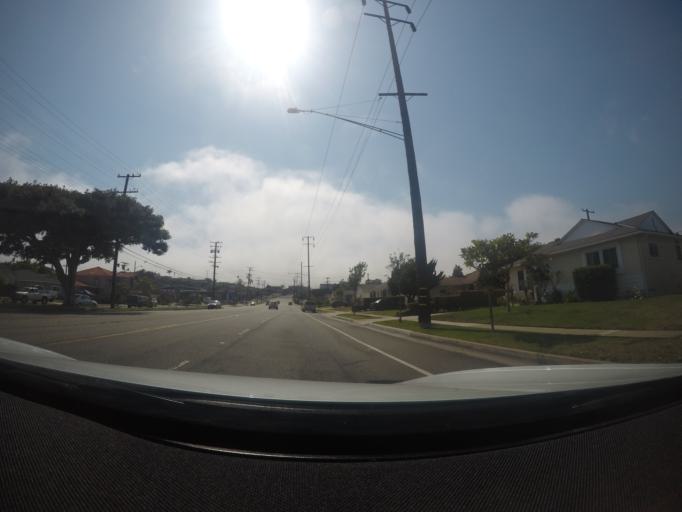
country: US
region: California
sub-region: Los Angeles County
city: Torrance
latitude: 33.8269
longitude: -118.3677
